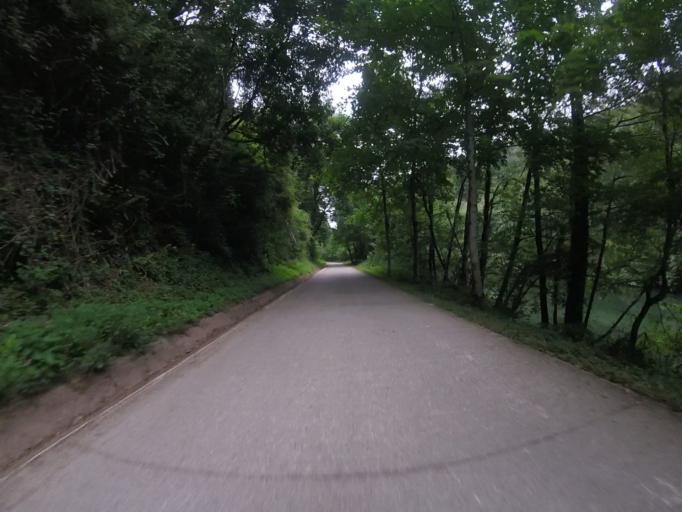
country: ES
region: Navarre
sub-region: Provincia de Navarra
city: Doneztebe
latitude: 43.1378
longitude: -1.6657
